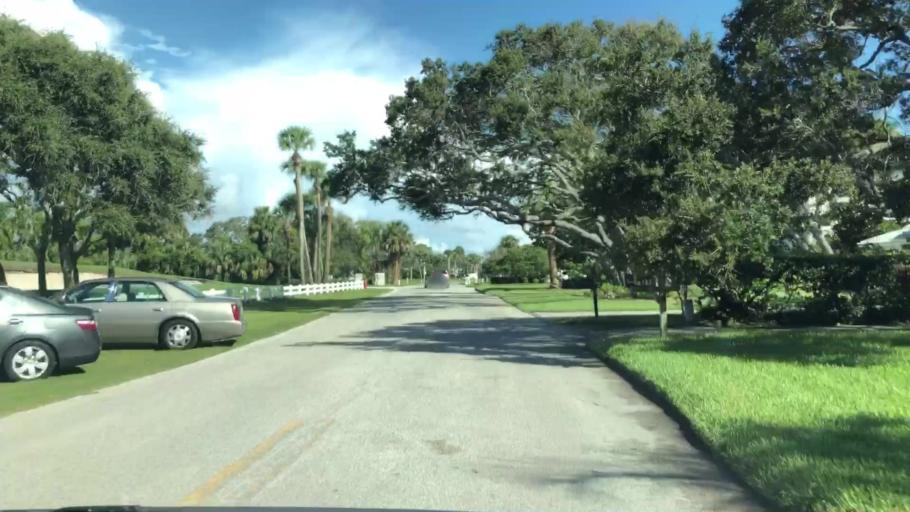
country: US
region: Florida
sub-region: Saint Johns County
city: Ponte Vedra Beach
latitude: 30.2383
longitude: -81.3806
